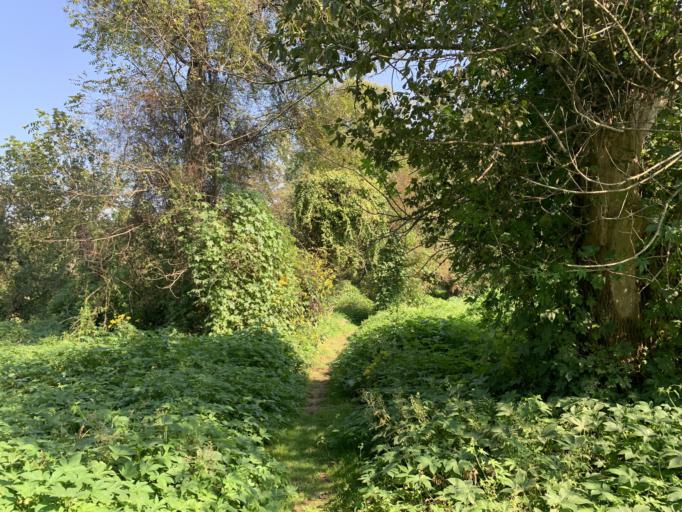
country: US
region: Maryland
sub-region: Harford County
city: Joppatowne
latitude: 39.4852
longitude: -76.3458
